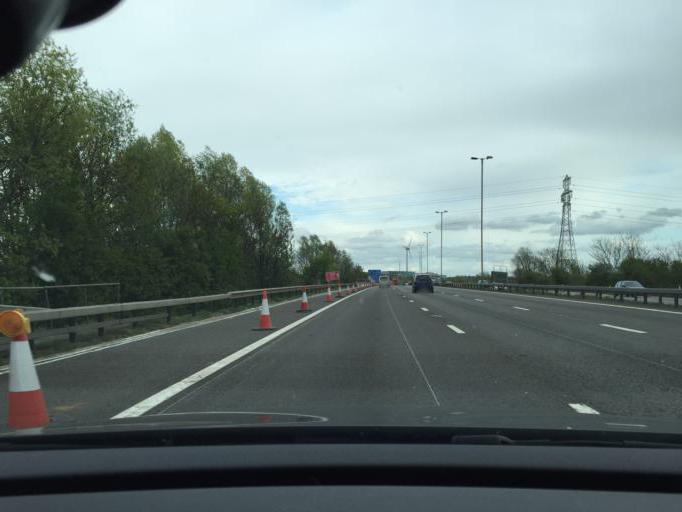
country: GB
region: England
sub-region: Reading
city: Reading
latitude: 51.4206
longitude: -1.0048
